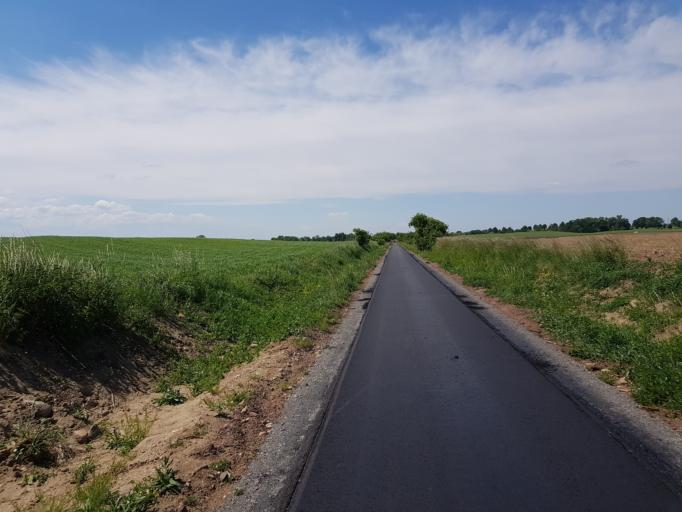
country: PL
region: West Pomeranian Voivodeship
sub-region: Powiat mysliborski
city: Barlinek
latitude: 52.9908
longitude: 15.1708
